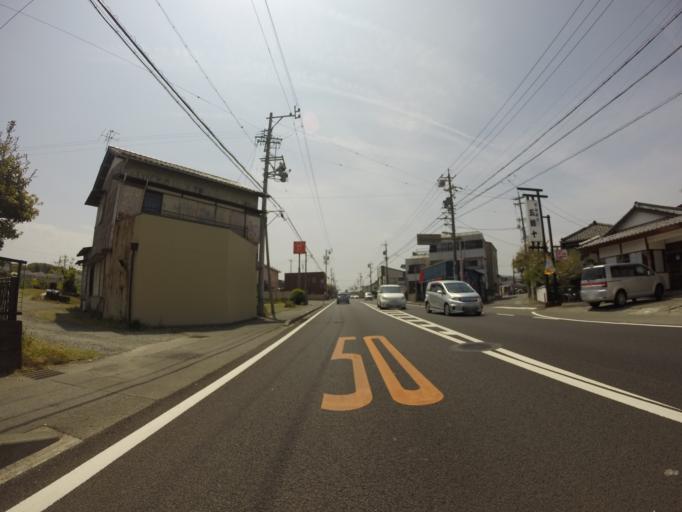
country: JP
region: Shizuoka
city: Shizuoka-shi
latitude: 35.0029
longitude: 138.5185
